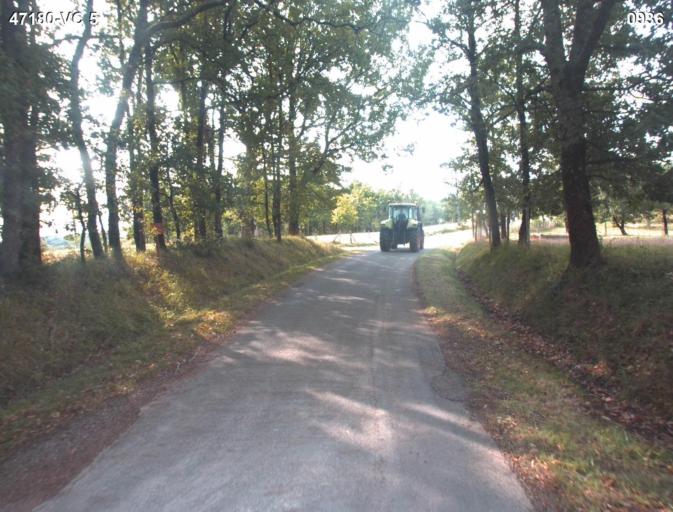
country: FR
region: Aquitaine
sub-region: Departement du Lot-et-Garonne
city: Sainte-Colombe-en-Bruilhois
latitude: 44.1748
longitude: 0.4688
